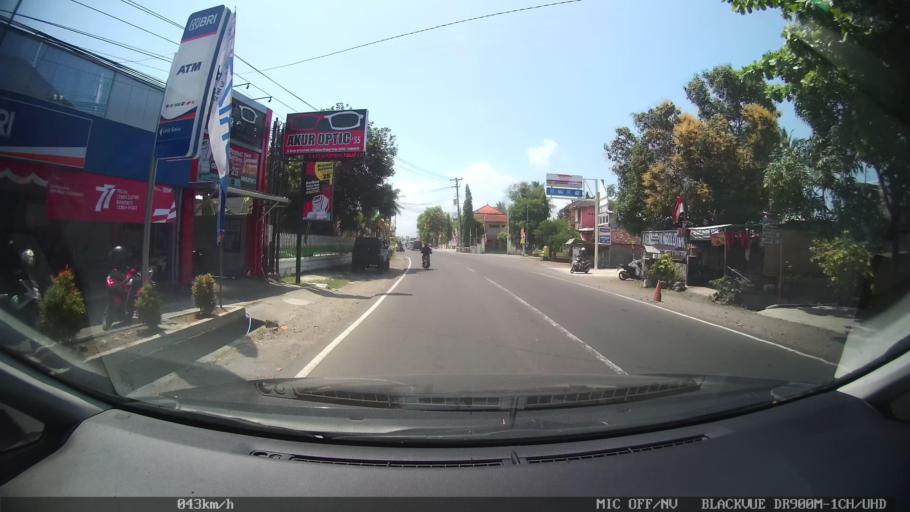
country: ID
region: Daerah Istimewa Yogyakarta
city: Srandakan
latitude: -7.9402
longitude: 110.2386
